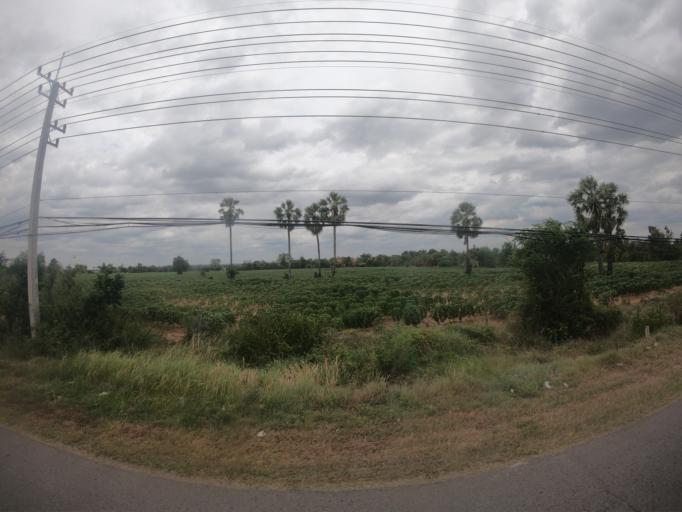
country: TH
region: Nakhon Ratchasima
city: Chok Chai
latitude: 14.8227
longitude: 102.1801
